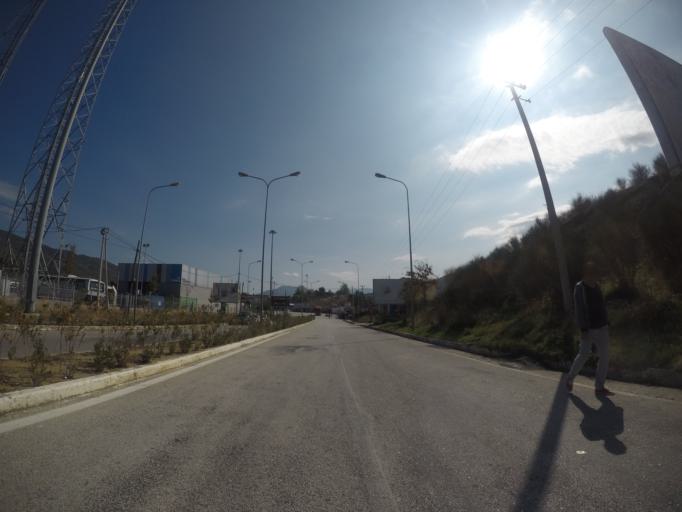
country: AL
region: Gjirokaster
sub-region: Rrethi i Gjirokastres
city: Kakavije
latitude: 39.9128
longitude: 20.3540
